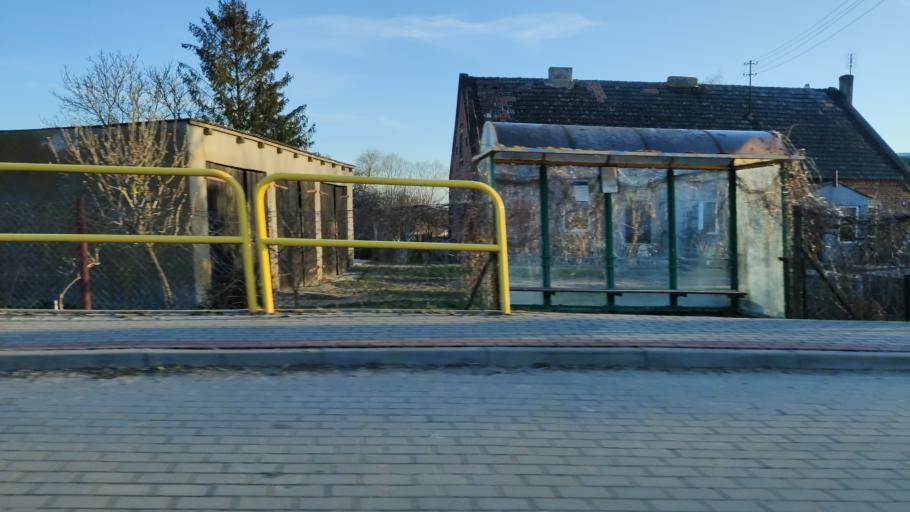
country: PL
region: Kujawsko-Pomorskie
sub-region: Powiat zninski
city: Barcin
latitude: 52.8777
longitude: 17.8832
